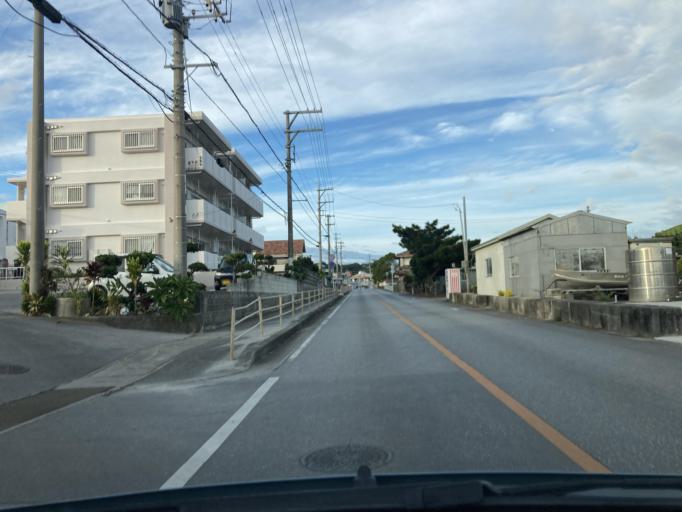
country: JP
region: Okinawa
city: Itoman
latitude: 26.1416
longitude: 127.6887
